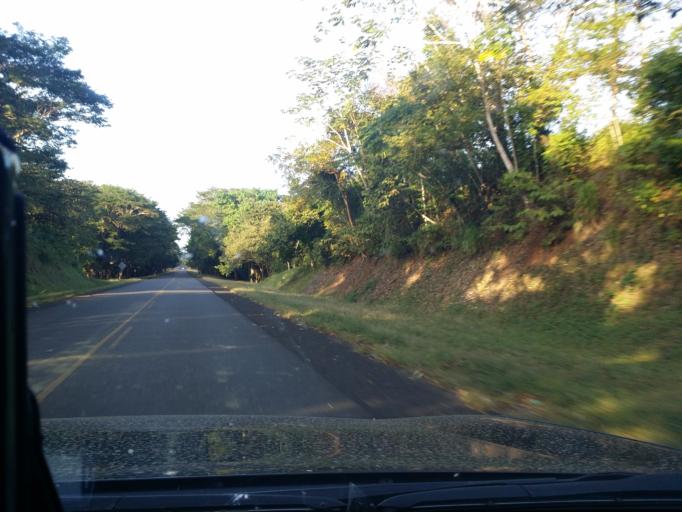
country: NI
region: Rio San Juan
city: San Miguelito
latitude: 11.4352
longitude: -84.8523
